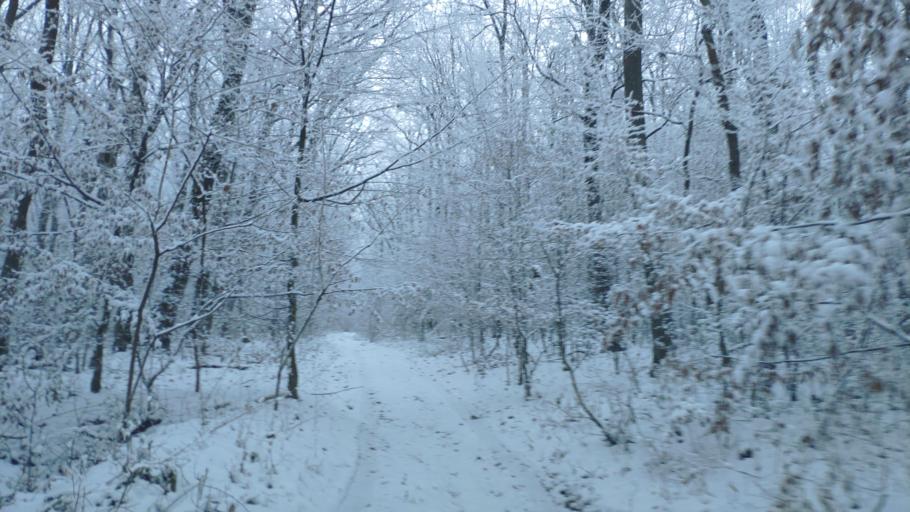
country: SK
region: Kosicky
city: Kosice
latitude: 48.6459
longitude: 21.1797
